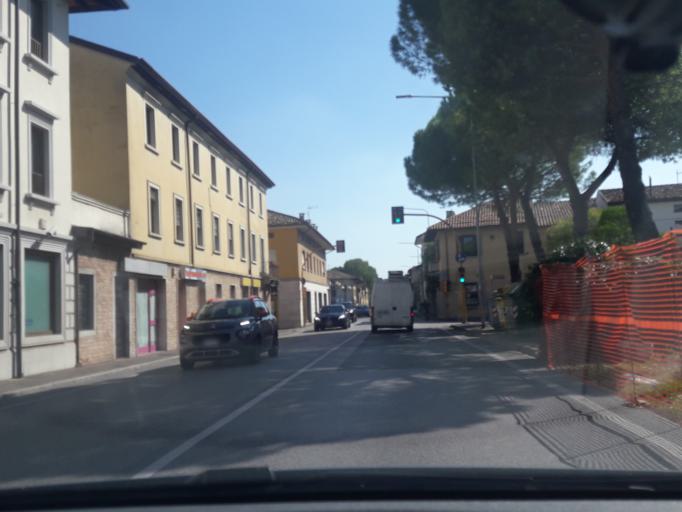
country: IT
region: Friuli Venezia Giulia
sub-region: Provincia di Udine
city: Feletto Umberto
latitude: 46.0868
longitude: 13.2329
